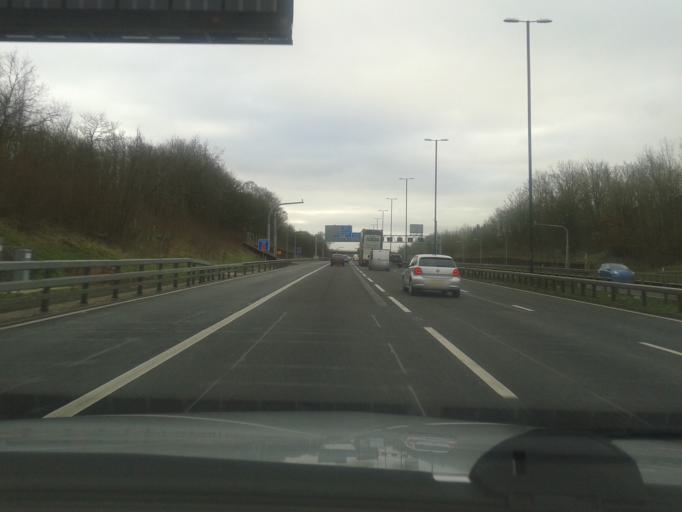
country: GB
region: England
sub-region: South Gloucestershire
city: Stoke Gifford
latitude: 51.5296
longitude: -2.5315
